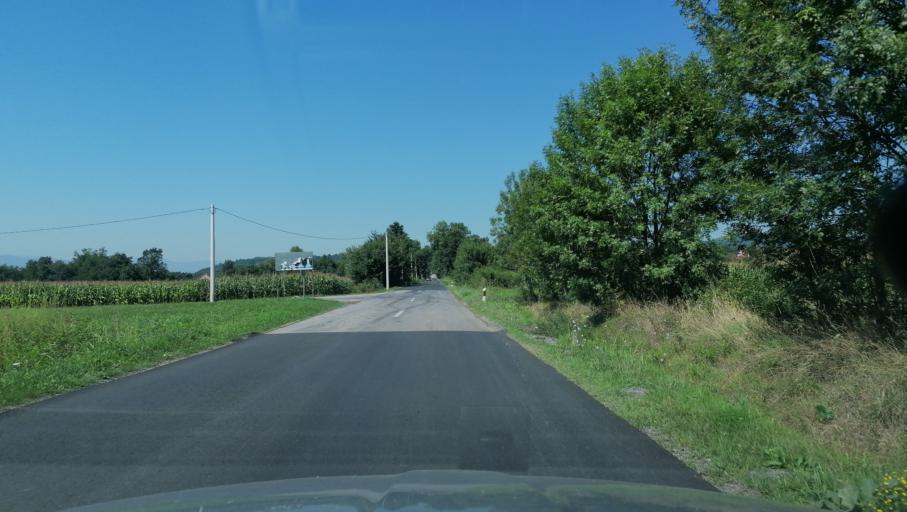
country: RS
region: Central Serbia
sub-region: Raski Okrug
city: Vrnjacka Banja
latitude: 43.7166
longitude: 20.8166
